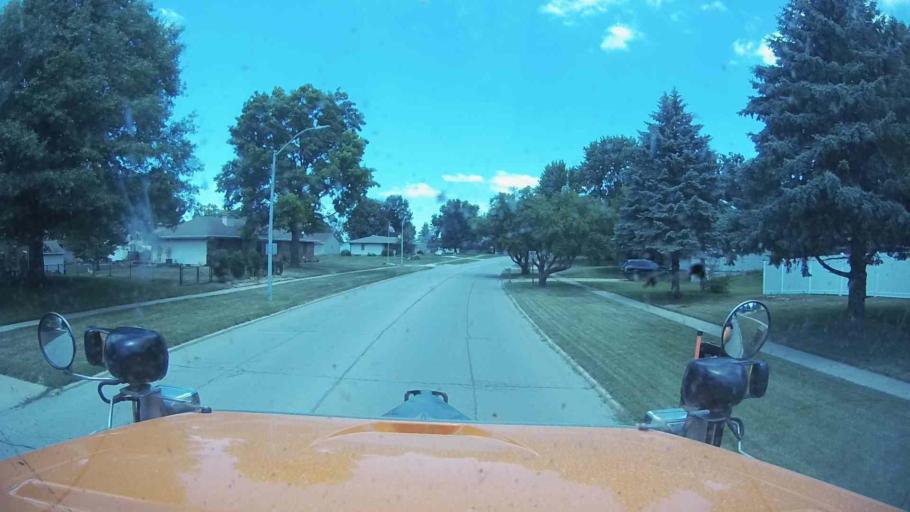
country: US
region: Iowa
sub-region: Polk County
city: Altoona
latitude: 41.6564
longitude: -93.4697
